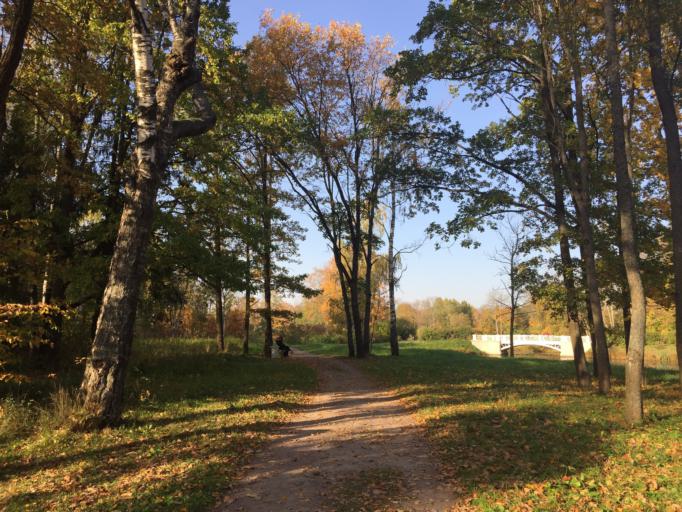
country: RU
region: St.-Petersburg
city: Pushkin
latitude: 59.7214
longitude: 30.3719
